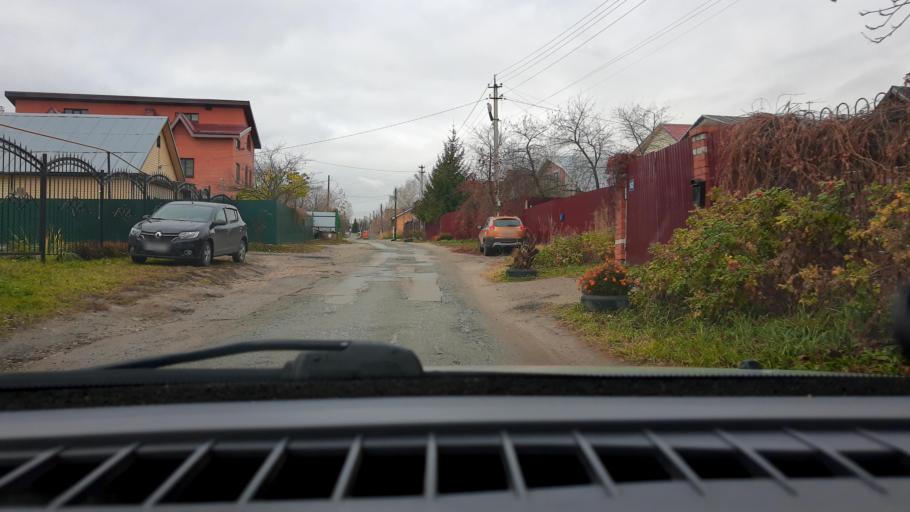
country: RU
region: Nizjnij Novgorod
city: Afonino
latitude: 56.1923
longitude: 44.0925
